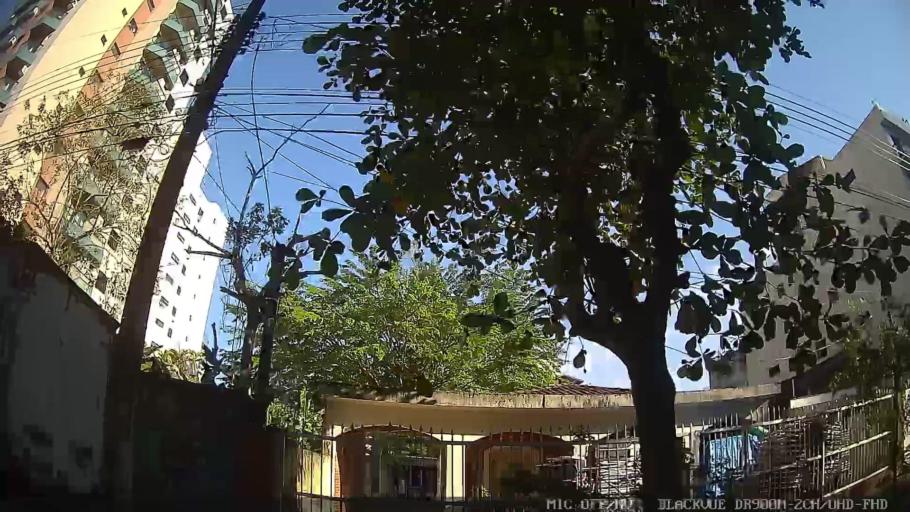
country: BR
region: Sao Paulo
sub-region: Guaruja
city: Guaruja
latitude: -24.0071
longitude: -46.2723
